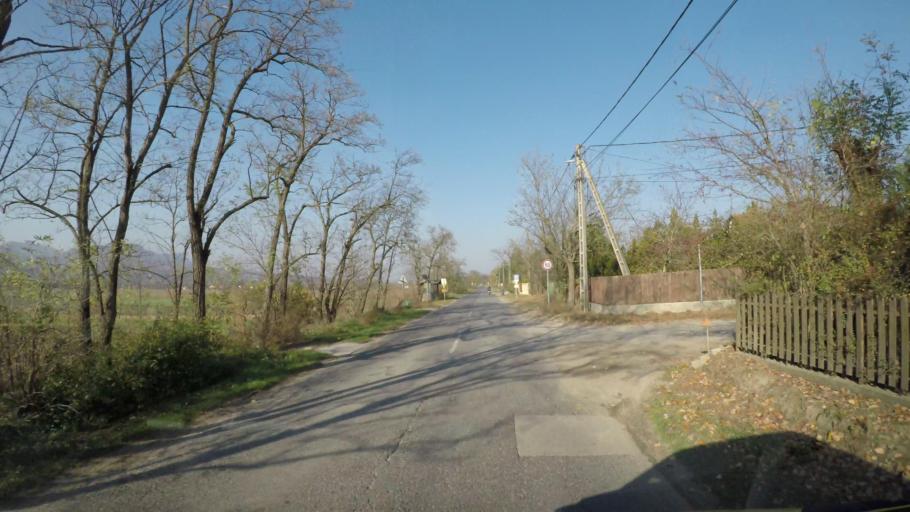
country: HU
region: Pest
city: Leanyfalu
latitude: 47.7078
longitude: 19.1070
